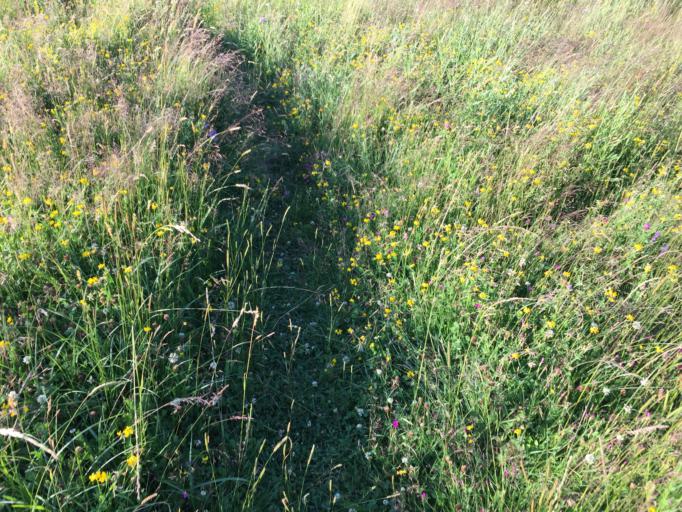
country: DE
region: Bavaria
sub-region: Regierungsbezirk Mittelfranken
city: Erlangen
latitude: 49.5696
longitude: 11.0094
